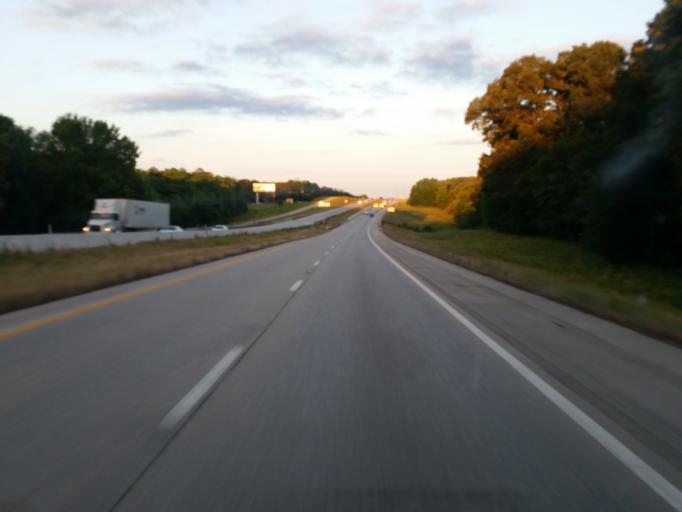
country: US
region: Texas
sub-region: Van Zandt County
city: Van
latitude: 32.4956
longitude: -95.5703
